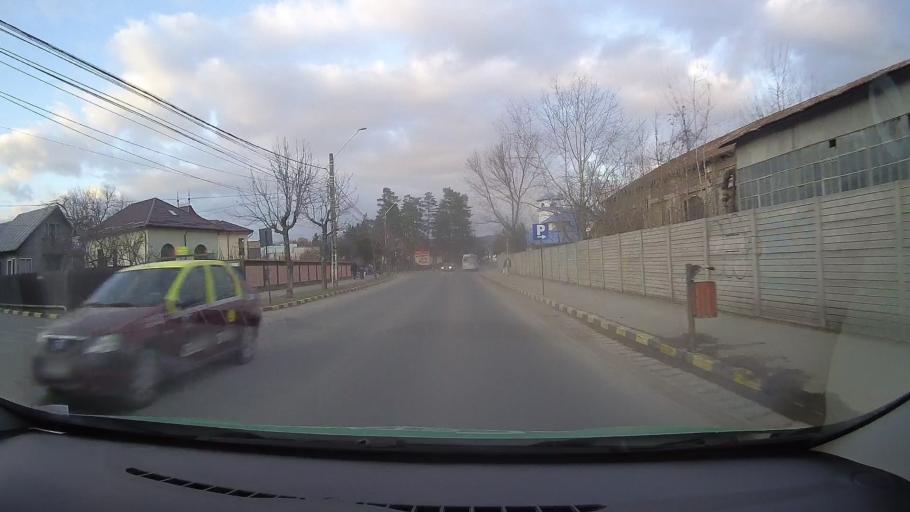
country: RO
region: Dambovita
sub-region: Municipiul Moreni
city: Moreni
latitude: 44.9812
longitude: 25.6388
